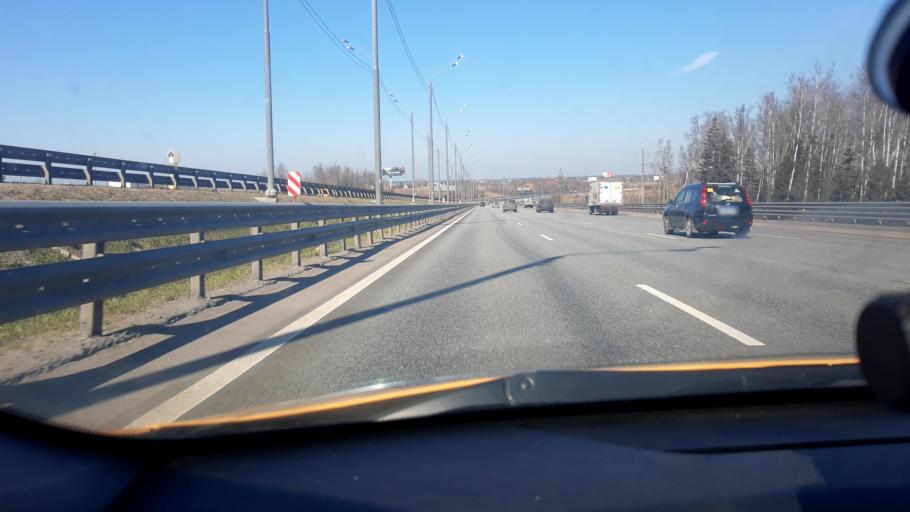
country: RU
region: Moskovskaya
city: Pavlovskaya Sloboda
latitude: 55.7857
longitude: 37.0757
